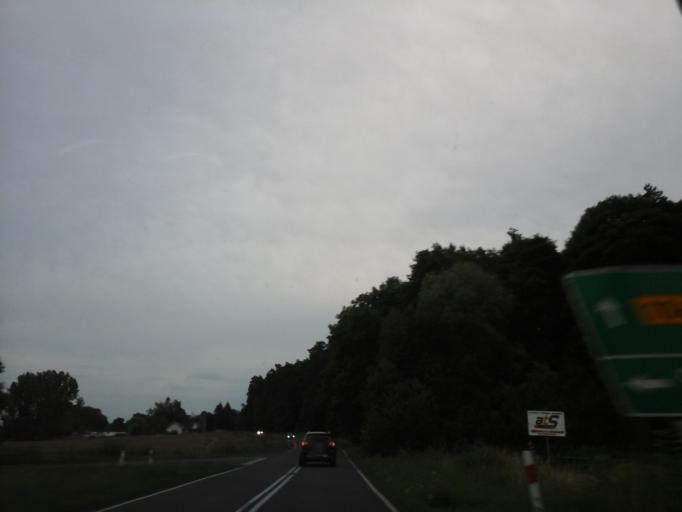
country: PL
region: West Pomeranian Voivodeship
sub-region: Powiat stargardzki
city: Stara Dabrowa
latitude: 53.4064
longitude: 15.0991
